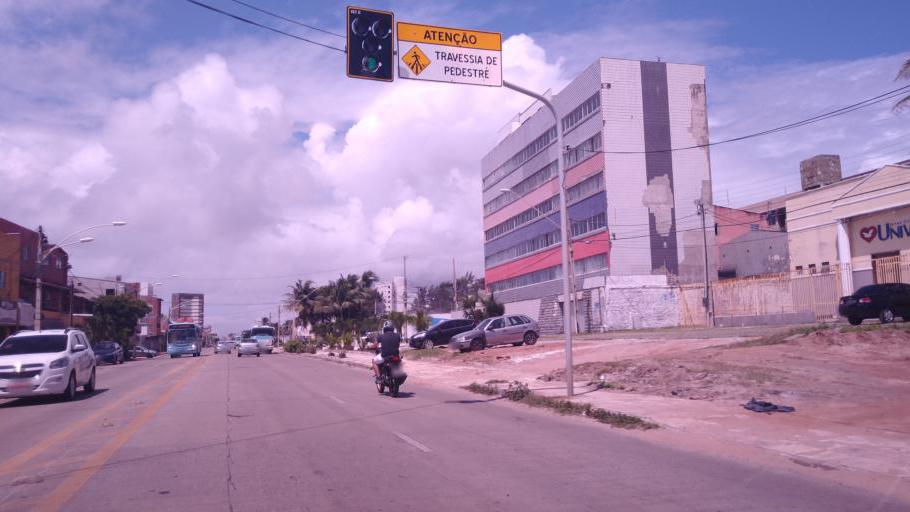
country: BR
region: Ceara
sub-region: Fortaleza
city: Fortaleza
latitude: -3.7258
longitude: -38.4620
